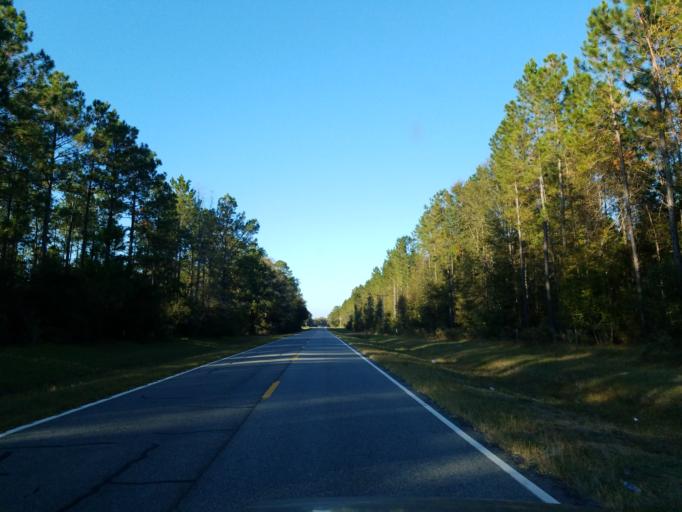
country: US
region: Georgia
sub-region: Lanier County
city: Lakeland
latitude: 30.9619
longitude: -83.0820
